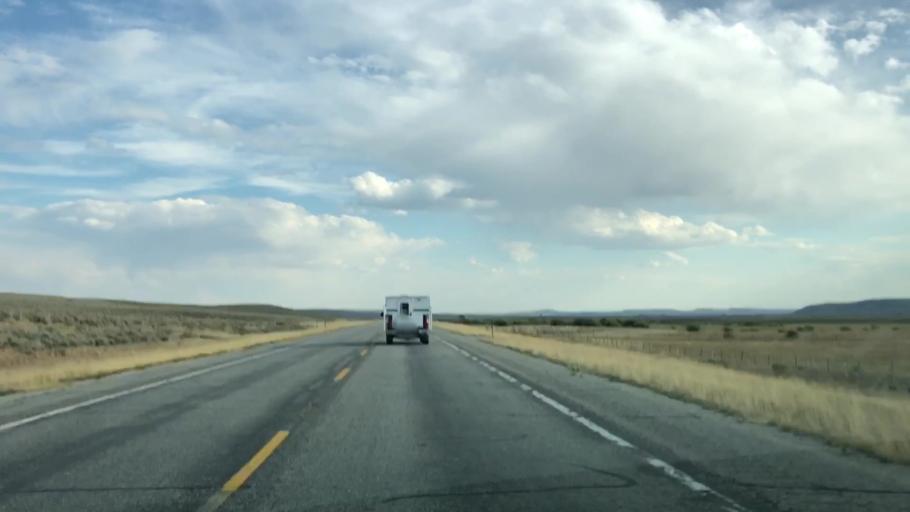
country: US
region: Wyoming
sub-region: Sublette County
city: Pinedale
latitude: 43.0283
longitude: -110.1260
